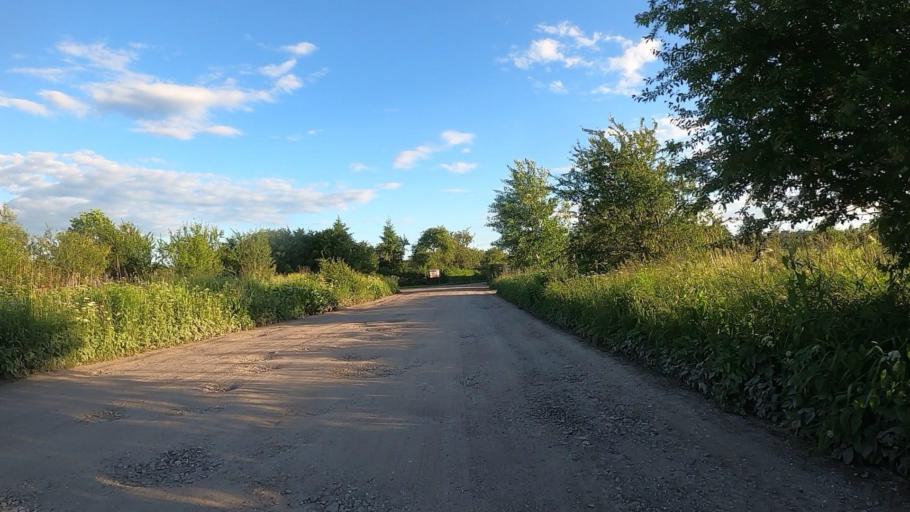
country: LV
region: Kekava
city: Kekava
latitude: 56.8830
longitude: 24.2216
